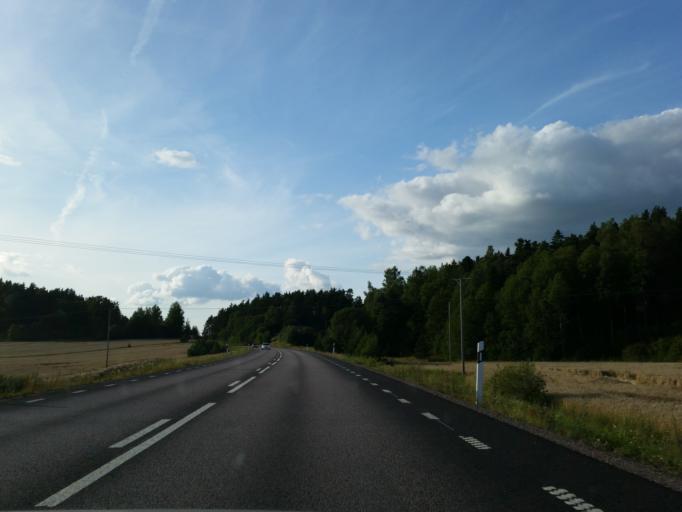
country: SE
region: Soedermanland
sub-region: Gnesta Kommun
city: Gnesta
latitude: 59.0431
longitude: 17.2921
